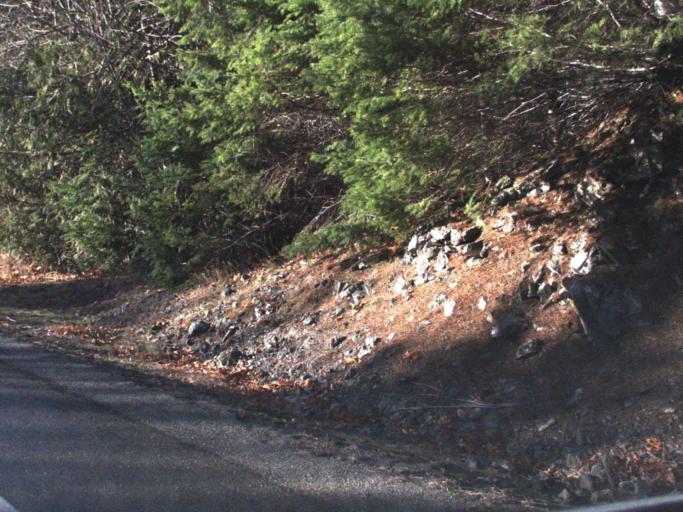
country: US
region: Washington
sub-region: Snohomish County
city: Darrington
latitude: 48.5742
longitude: -121.4085
